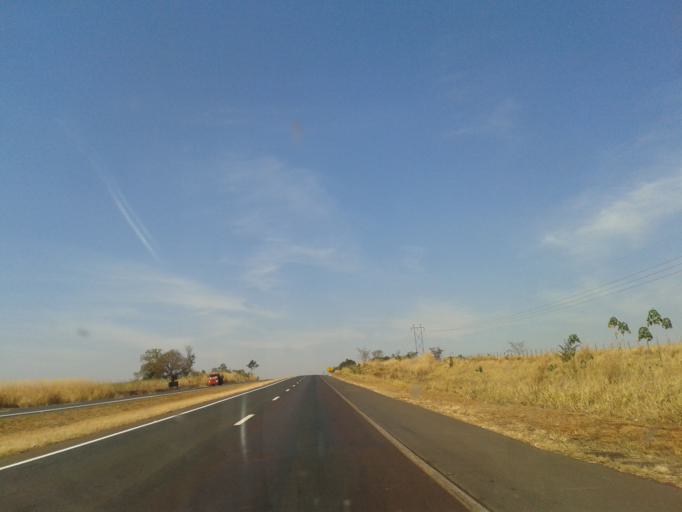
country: BR
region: Goias
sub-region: Goiatuba
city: Goiatuba
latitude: -18.1909
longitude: -49.2861
